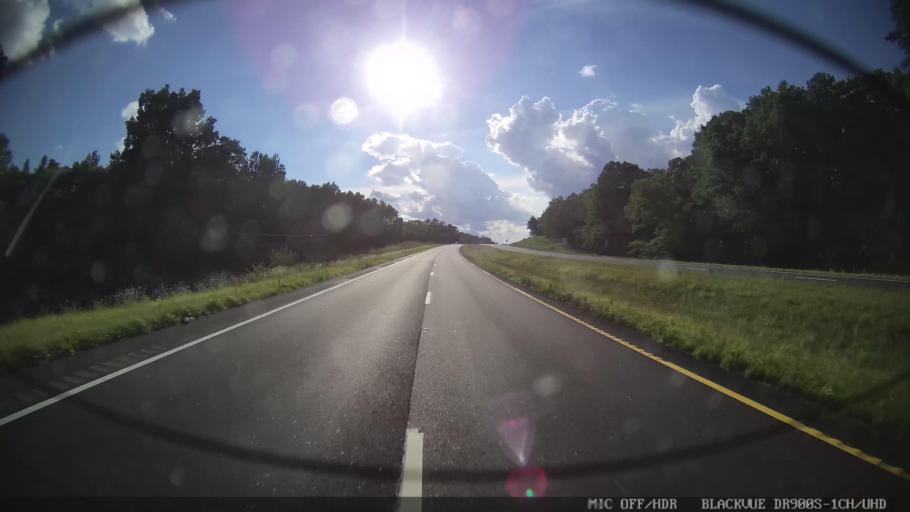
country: US
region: Georgia
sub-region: Floyd County
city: Lindale
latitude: 34.2067
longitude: -85.0862
